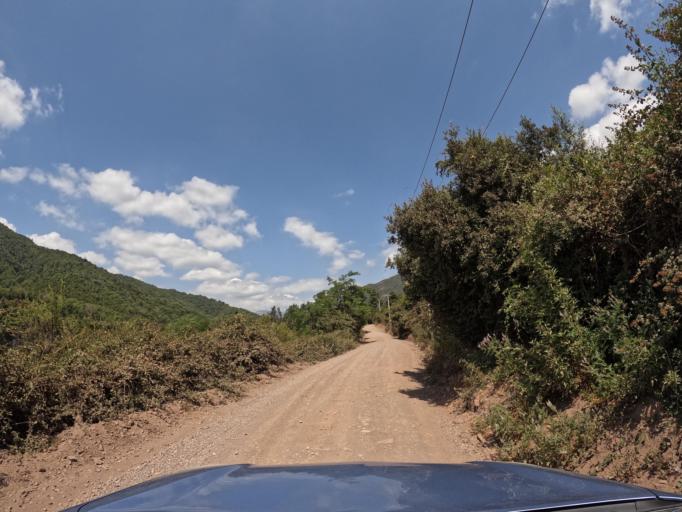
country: CL
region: Maule
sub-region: Provincia de Curico
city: Curico
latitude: -35.1226
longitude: -71.0039
